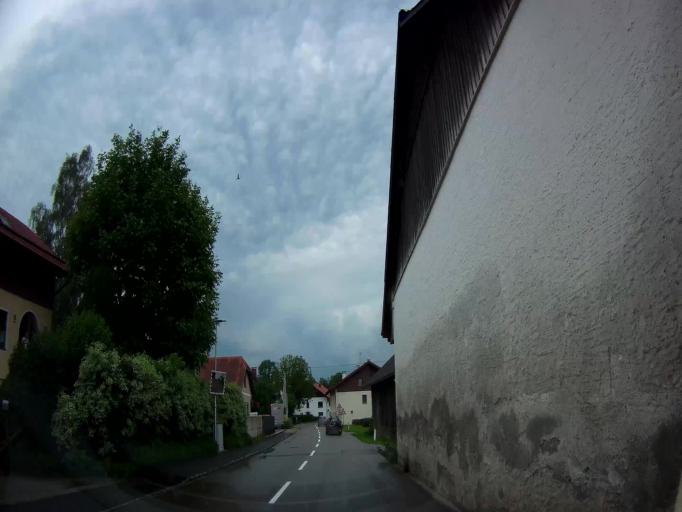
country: AT
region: Salzburg
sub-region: Politischer Bezirk Salzburg-Umgebung
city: Mattsee
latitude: 48.0789
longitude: 13.1456
